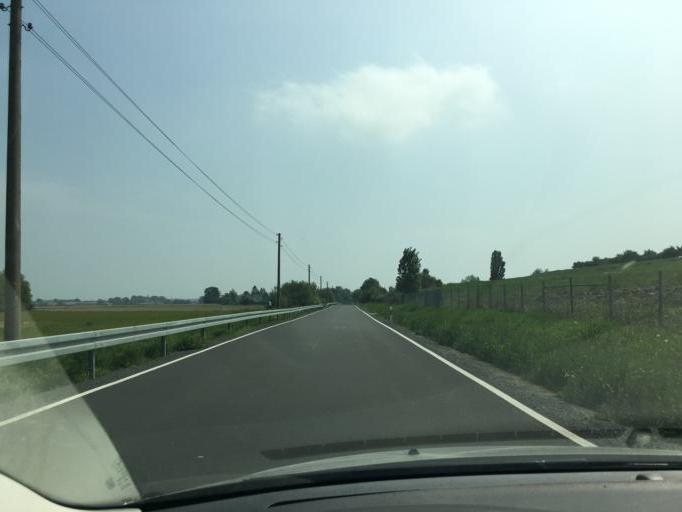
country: DE
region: Saxony
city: Grossposna
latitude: 51.2951
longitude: 12.4960
